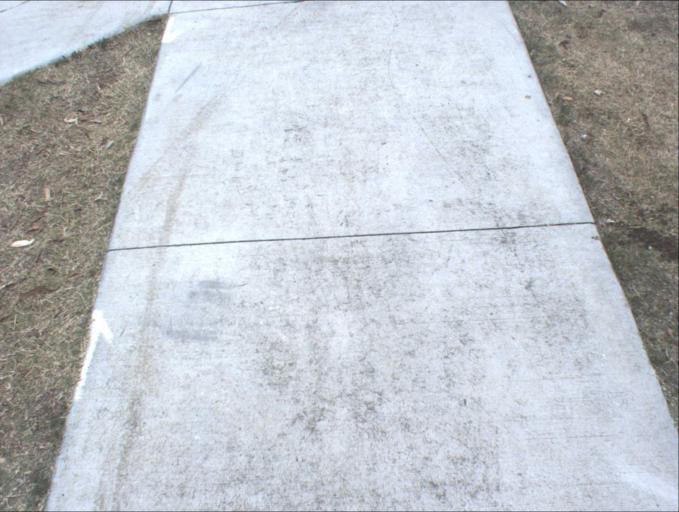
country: AU
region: Queensland
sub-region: Logan
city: Slacks Creek
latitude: -27.6631
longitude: 153.1682
